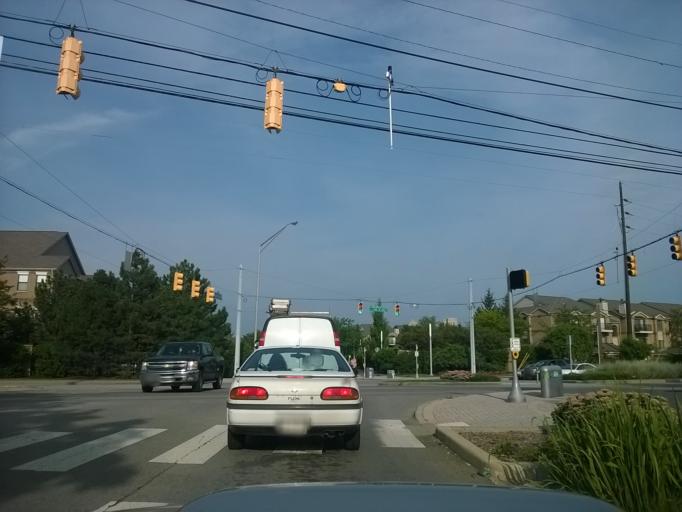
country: US
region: Indiana
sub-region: Marion County
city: Indianapolis
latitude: 39.7783
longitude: -86.1680
